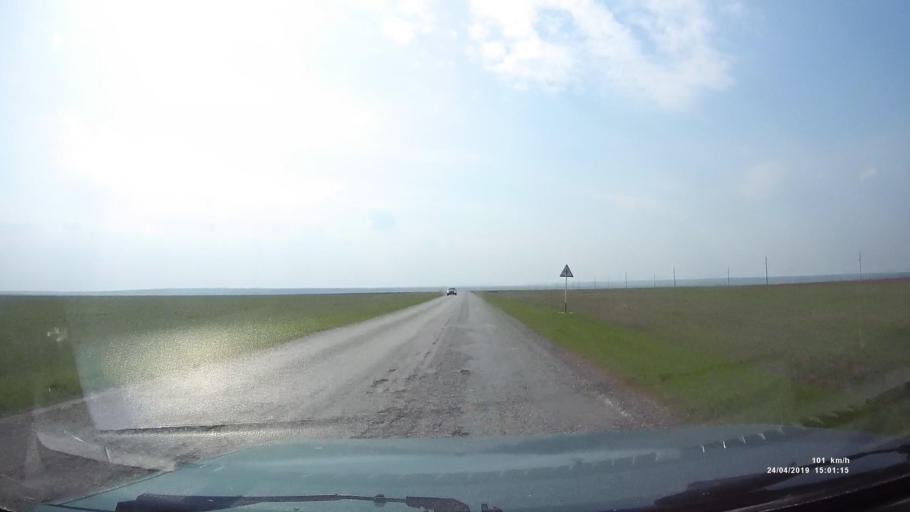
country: RU
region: Rostov
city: Remontnoye
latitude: 46.5657
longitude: 43.5377
